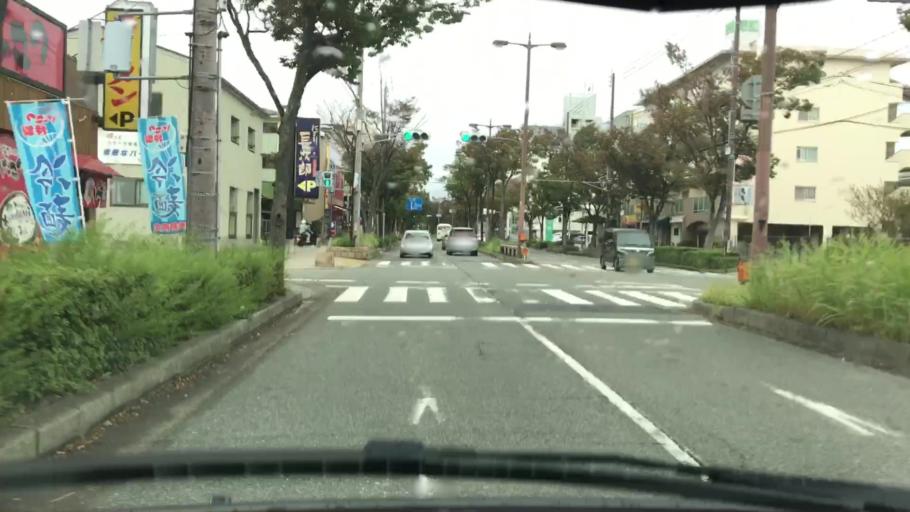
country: JP
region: Hyogo
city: Amagasaki
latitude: 34.7445
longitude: 135.3956
